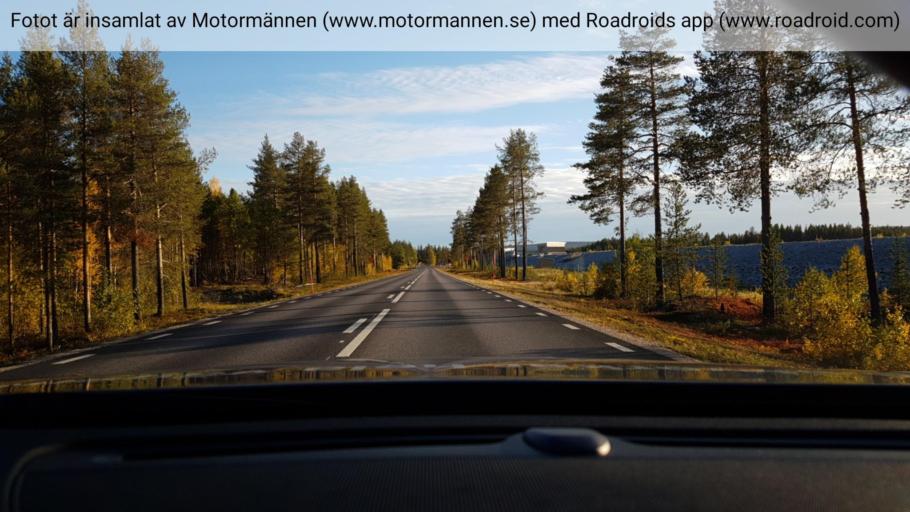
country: SE
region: Norrbotten
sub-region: Jokkmokks Kommun
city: Jokkmokk
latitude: 66.6358
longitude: 19.8237
